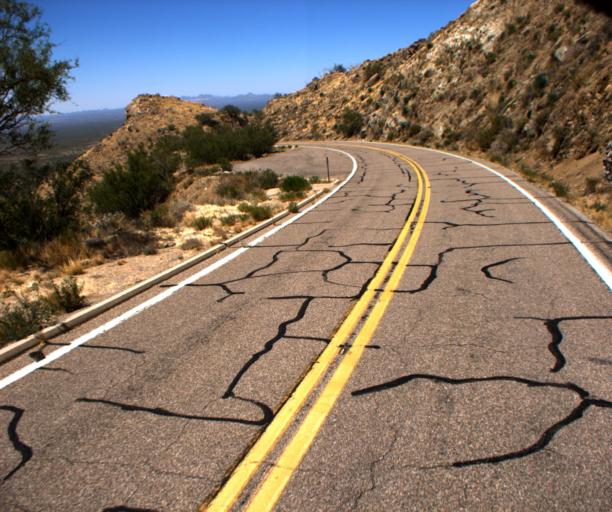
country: US
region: Arizona
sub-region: Pima County
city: Sells
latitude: 31.9864
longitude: -111.6001
